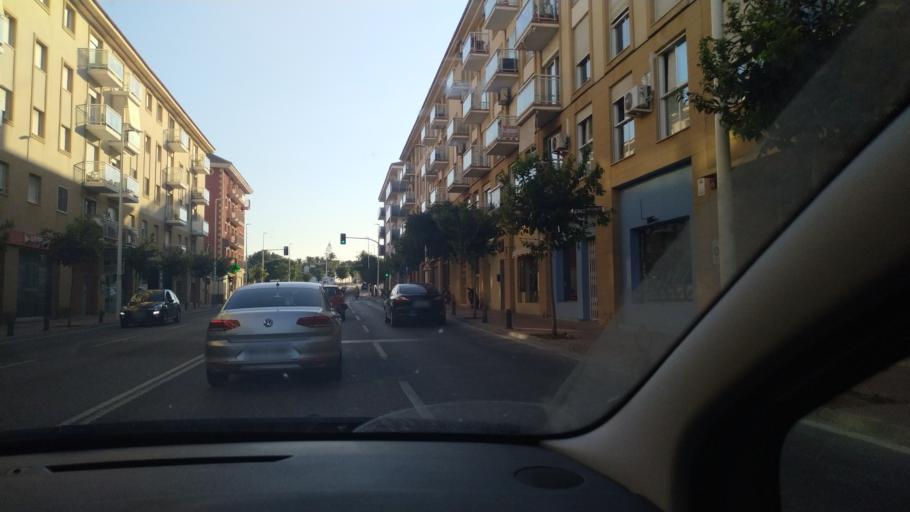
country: ES
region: Valencia
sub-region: Provincia de Alicante
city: Javea
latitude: 38.7859
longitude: 0.1636
